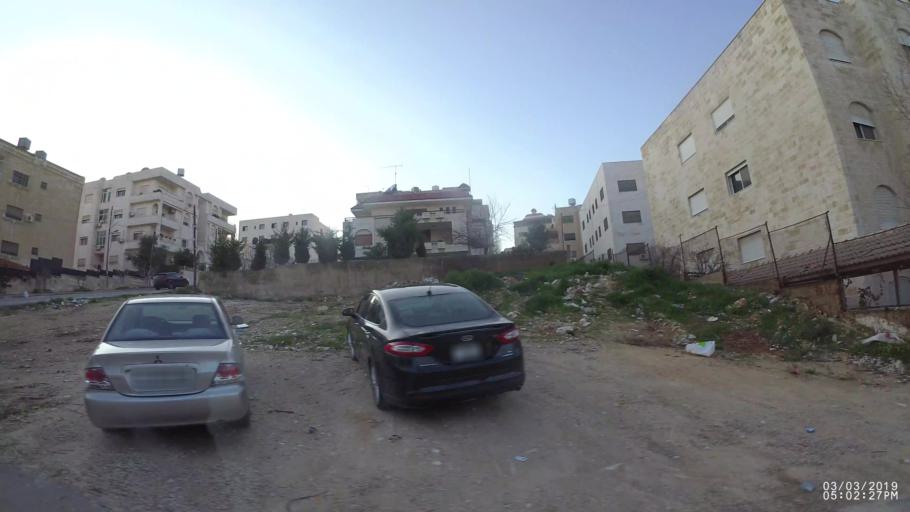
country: JO
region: Amman
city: Al Jubayhah
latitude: 31.9898
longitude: 35.8777
